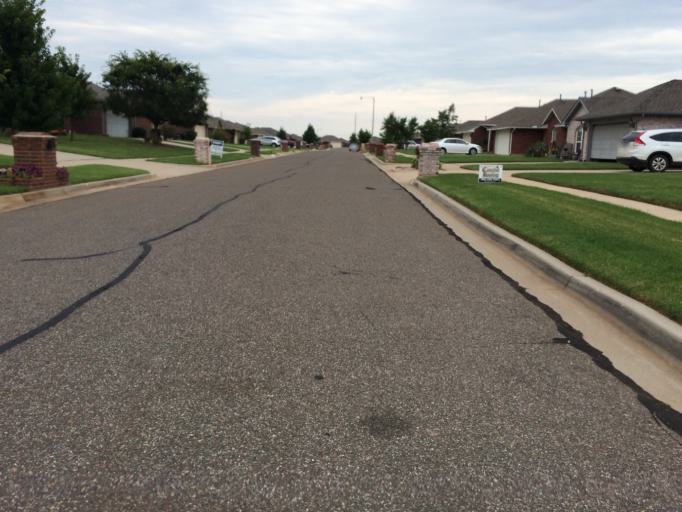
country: US
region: Oklahoma
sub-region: Cleveland County
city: Hall Park
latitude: 35.2509
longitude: -97.4200
